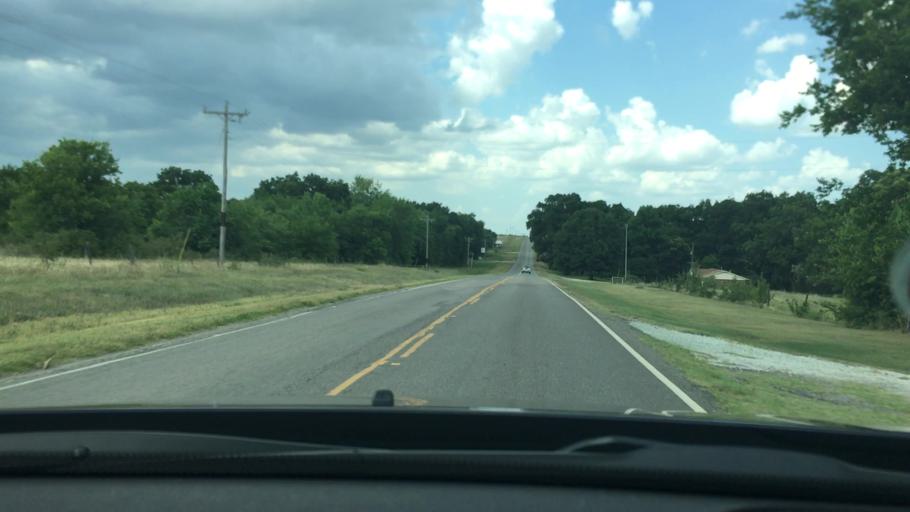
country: US
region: Oklahoma
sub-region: Pontotoc County
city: Ada
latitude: 34.5460
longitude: -96.6347
